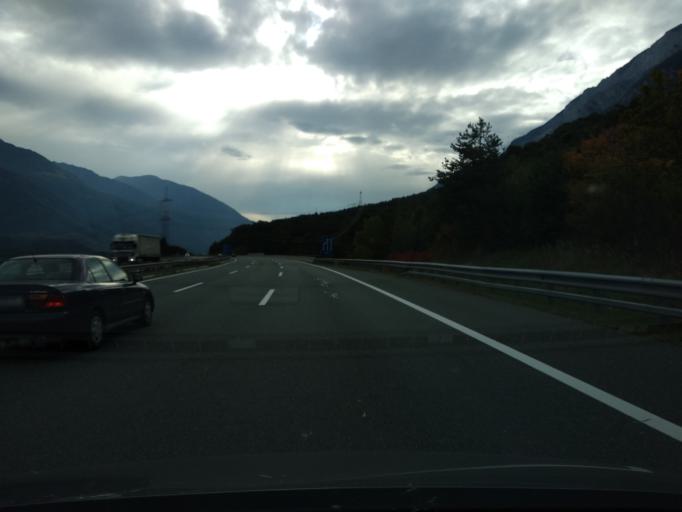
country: AT
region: Tyrol
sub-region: Politischer Bezirk Imst
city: Haiming
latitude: 47.2515
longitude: 10.8597
